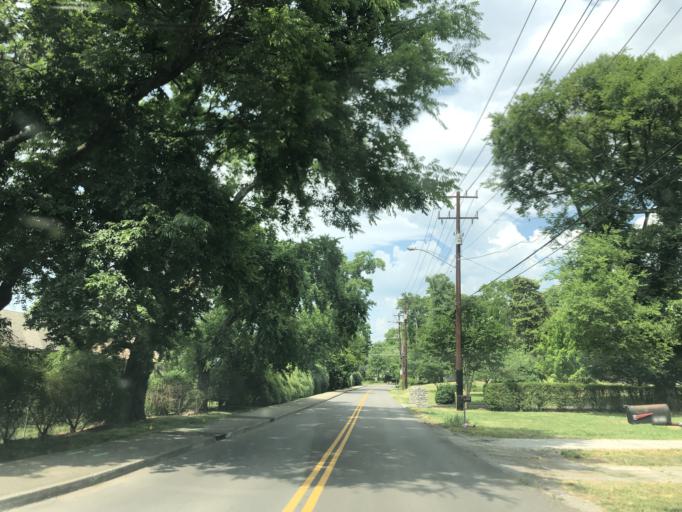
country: US
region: Tennessee
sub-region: Davidson County
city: Belle Meade
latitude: 36.1246
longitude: -86.8184
